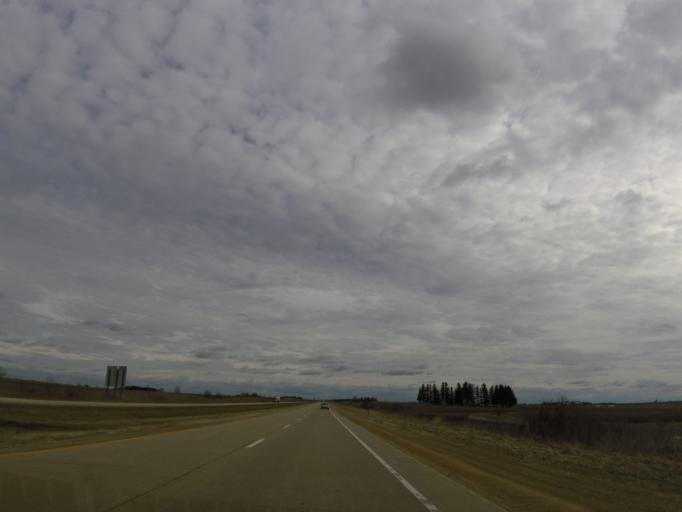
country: US
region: Iowa
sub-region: Chickasaw County
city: New Hampton
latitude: 43.0489
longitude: -92.3346
